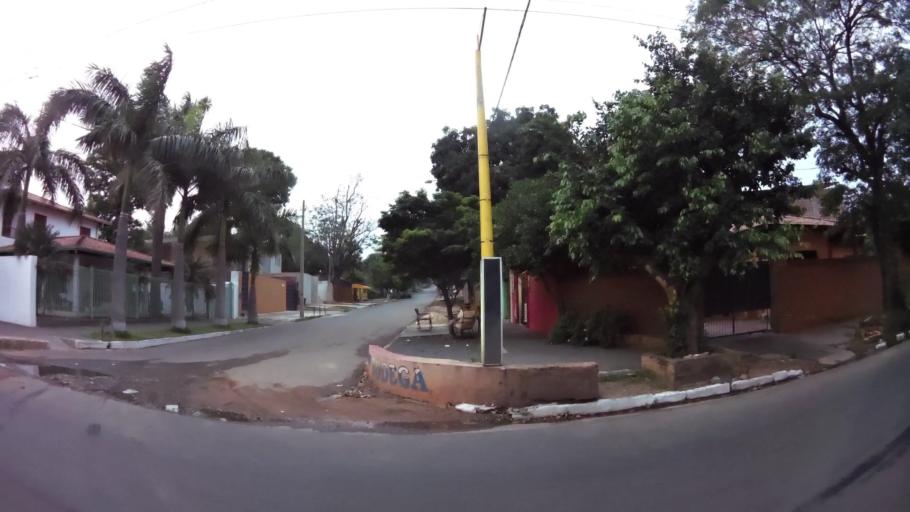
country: PY
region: Central
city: Lambare
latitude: -25.3339
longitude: -57.6085
